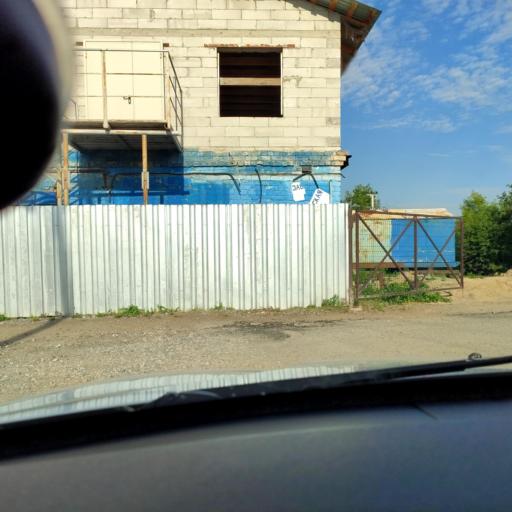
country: RU
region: Perm
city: Ferma
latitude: 57.8969
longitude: 56.2900
